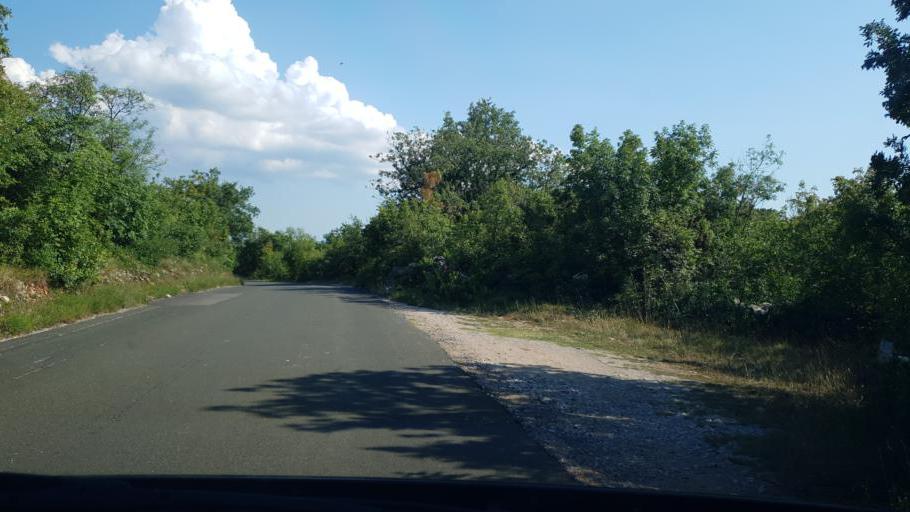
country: HR
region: Primorsko-Goranska
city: Omisalj
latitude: 45.1878
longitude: 14.5860
